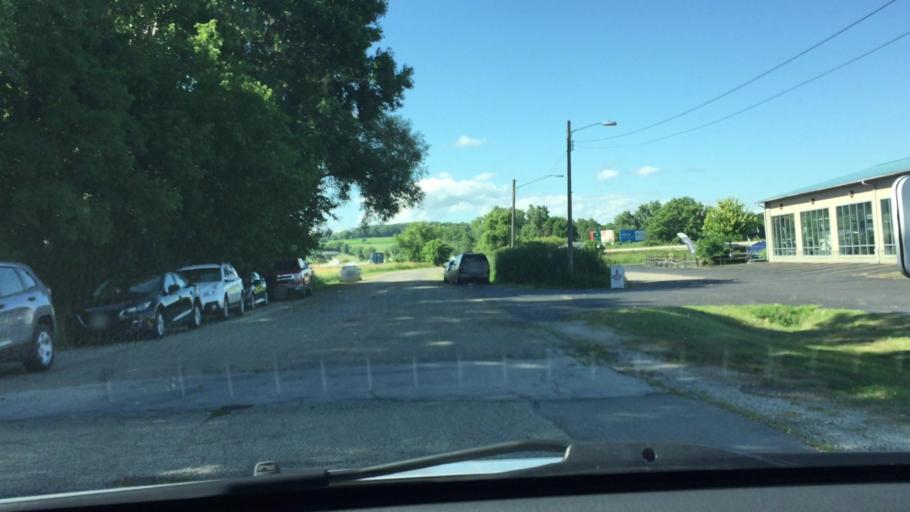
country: US
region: Wisconsin
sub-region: Waukesha County
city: Pewaukee
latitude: 43.0881
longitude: -88.2550
